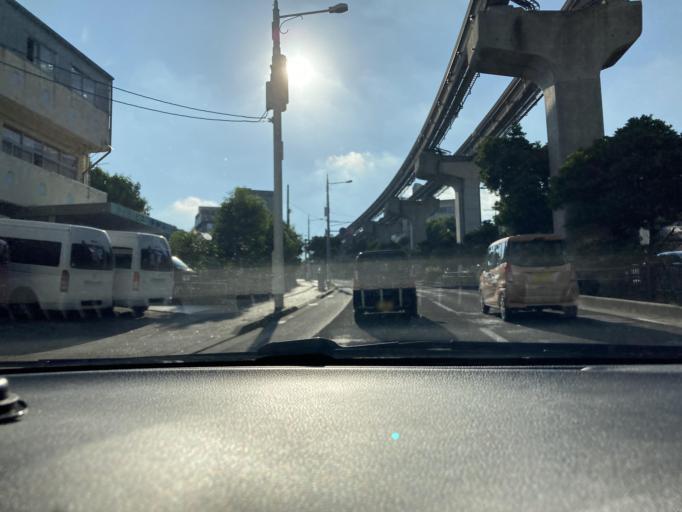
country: JP
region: Okinawa
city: Naha-shi
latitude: 26.2260
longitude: 127.7128
